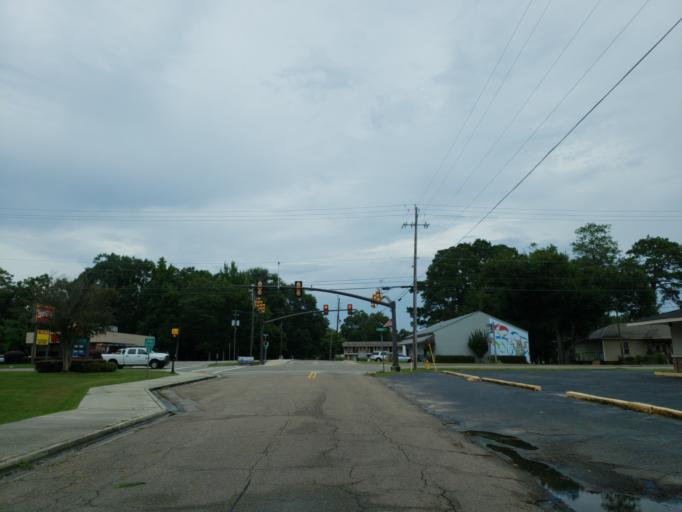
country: US
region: Mississippi
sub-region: Forrest County
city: Hattiesburg
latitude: 31.3242
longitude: -89.3143
